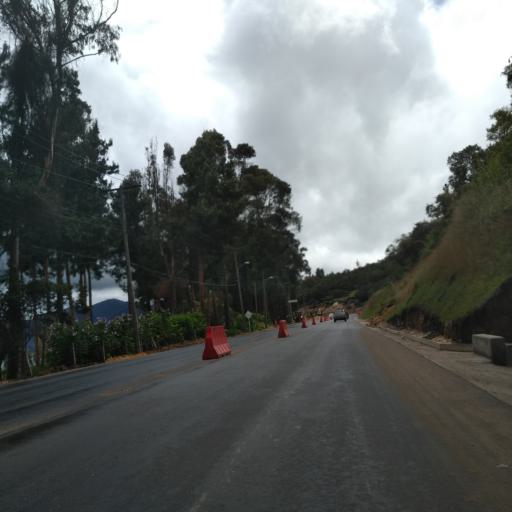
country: CO
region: Bogota D.C.
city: Barrio San Luis
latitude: 4.6848
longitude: -73.9896
